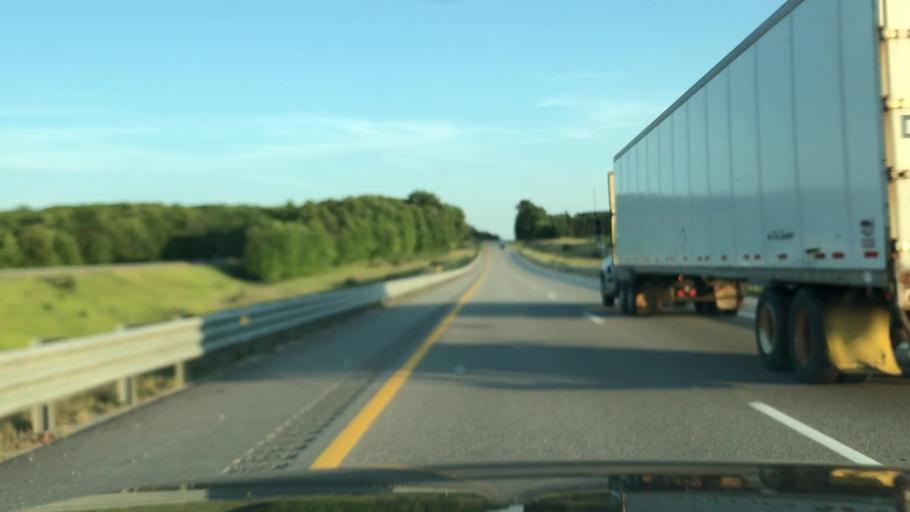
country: US
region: Michigan
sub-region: Osceola County
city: Reed City
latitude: 43.8578
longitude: -85.5347
